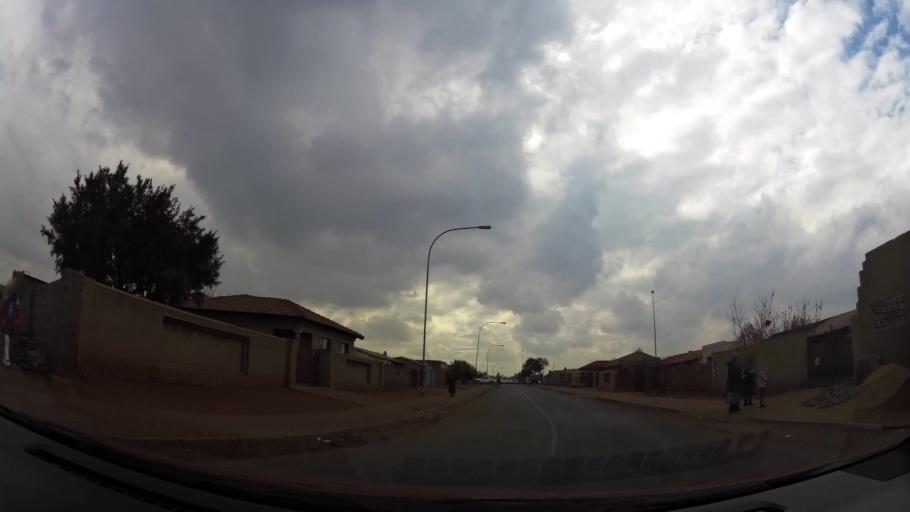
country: ZA
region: Gauteng
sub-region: City of Johannesburg Metropolitan Municipality
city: Soweto
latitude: -26.2554
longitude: 27.8296
